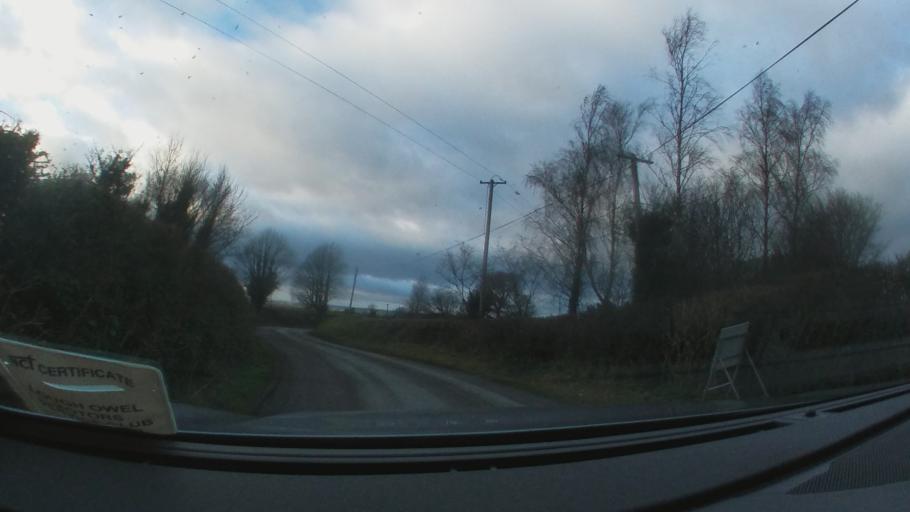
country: IE
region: Leinster
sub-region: Kilkenny
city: Thomastown
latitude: 52.5736
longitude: -7.1488
